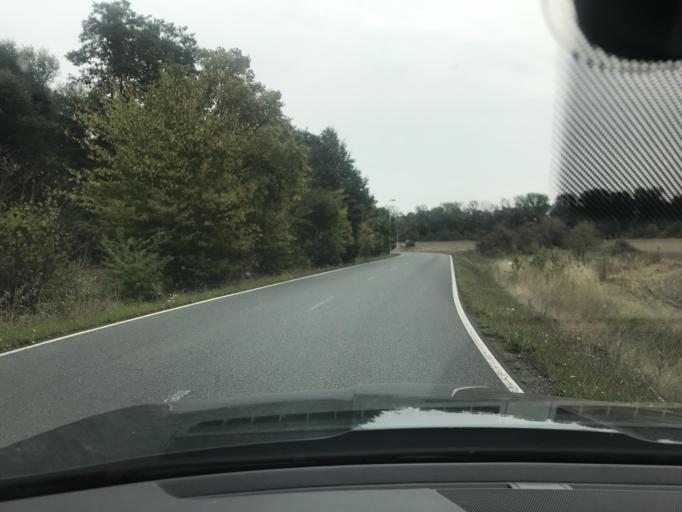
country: DE
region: Saxony-Anhalt
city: Ditfurt
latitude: 51.8041
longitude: 11.1848
